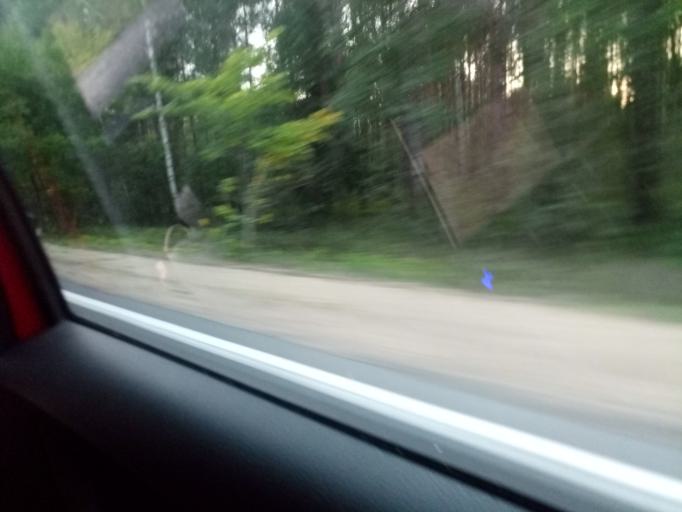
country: RU
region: Moskovskaya
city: Noginsk-9
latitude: 56.0956
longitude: 38.5822
